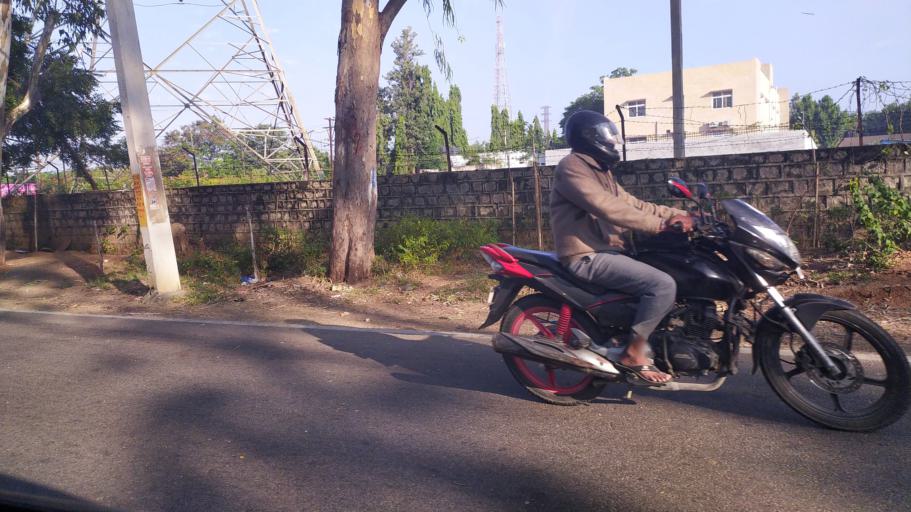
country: IN
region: Telangana
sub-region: Hyderabad
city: Hyderabad
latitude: 17.3298
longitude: 78.4100
